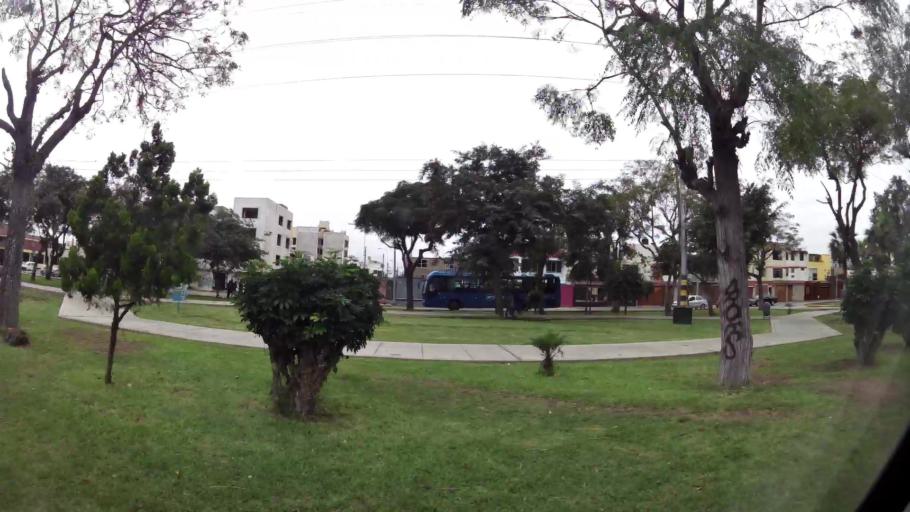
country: PE
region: Callao
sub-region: Callao
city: Callao
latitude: -12.0700
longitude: -77.0945
